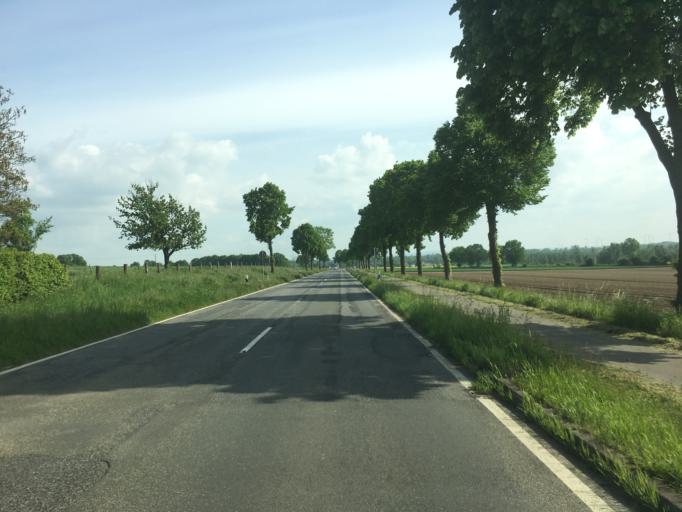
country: DE
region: North Rhine-Westphalia
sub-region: Regierungsbezirk Koln
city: Linnich
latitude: 50.9761
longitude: 6.3116
